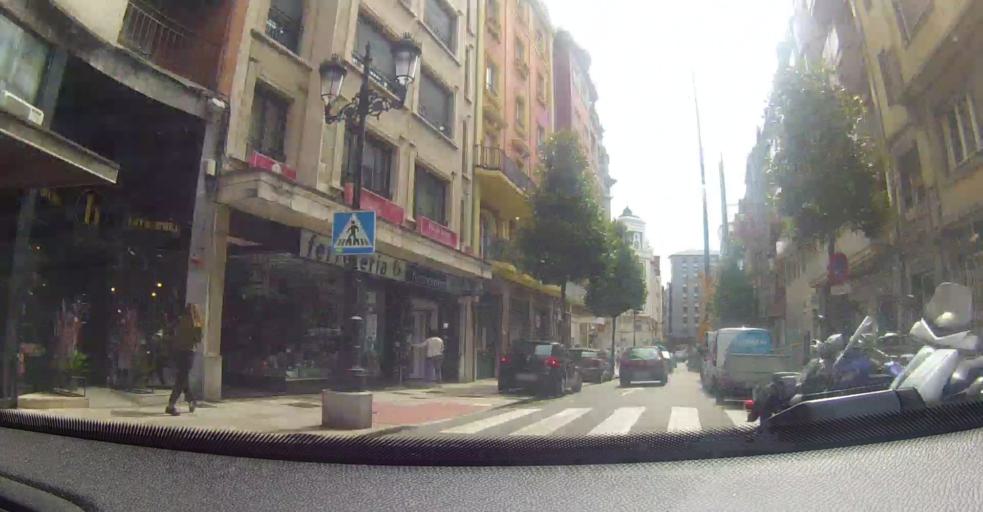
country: ES
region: Asturias
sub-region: Province of Asturias
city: Oviedo
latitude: 43.3650
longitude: -5.8516
